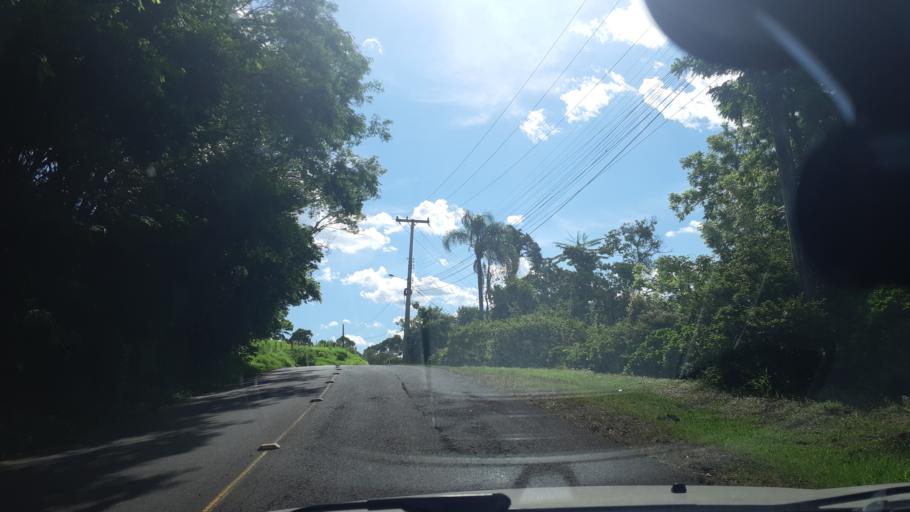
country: BR
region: Rio Grande do Sul
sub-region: Novo Hamburgo
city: Novo Hamburgo
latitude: -29.6259
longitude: -51.1023
